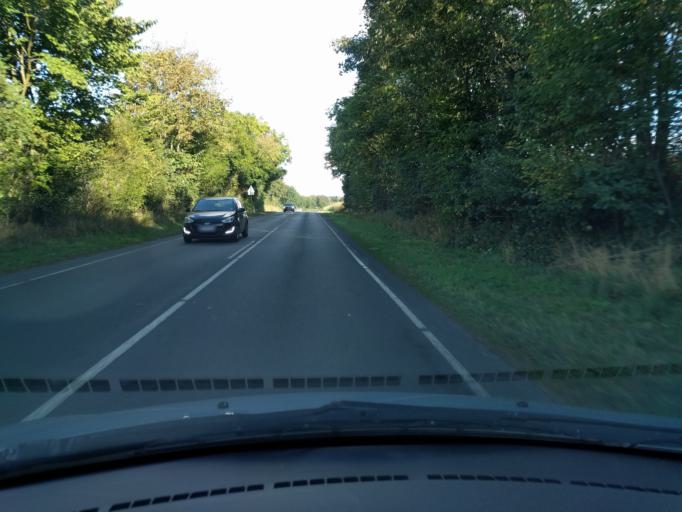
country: DK
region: South Denmark
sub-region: Assens Kommune
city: Glamsbjerg
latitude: 55.2690
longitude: 10.0908
